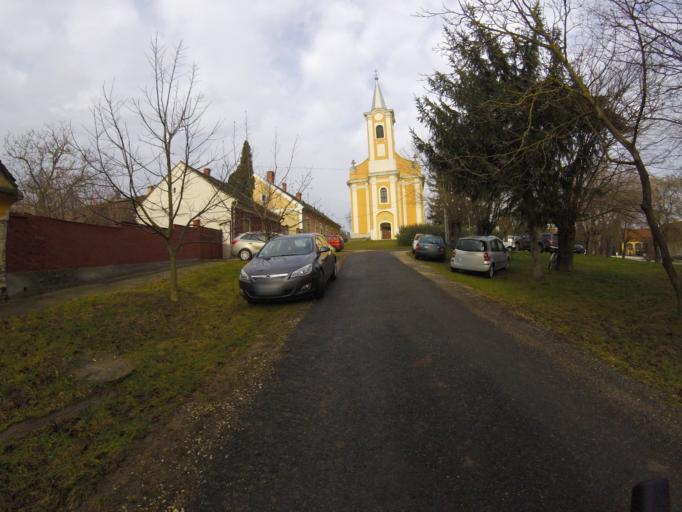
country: HU
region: Vas
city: Sarvar
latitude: 47.2460
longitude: 17.0255
